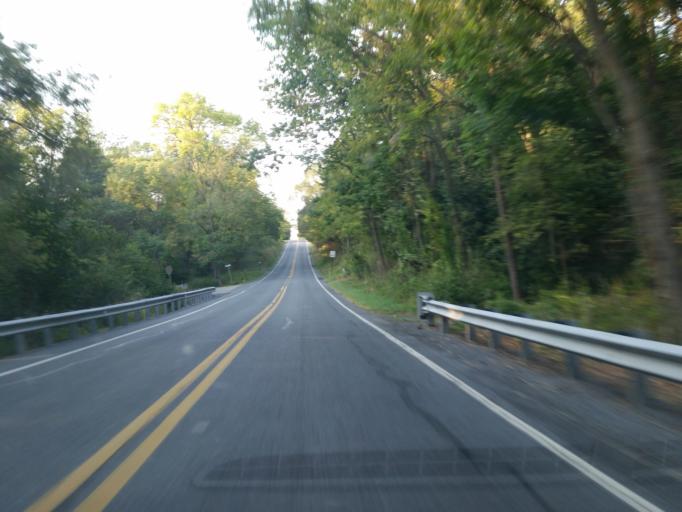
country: US
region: Pennsylvania
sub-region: Lebanon County
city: Annville
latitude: 40.3602
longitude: -76.5271
